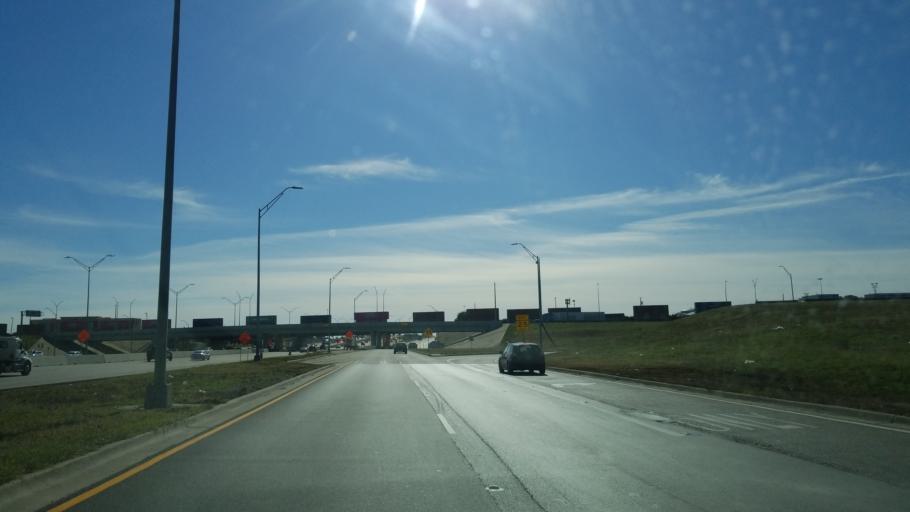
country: US
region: Texas
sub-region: Tarrant County
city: Arlington
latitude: 32.7451
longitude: -97.0630
